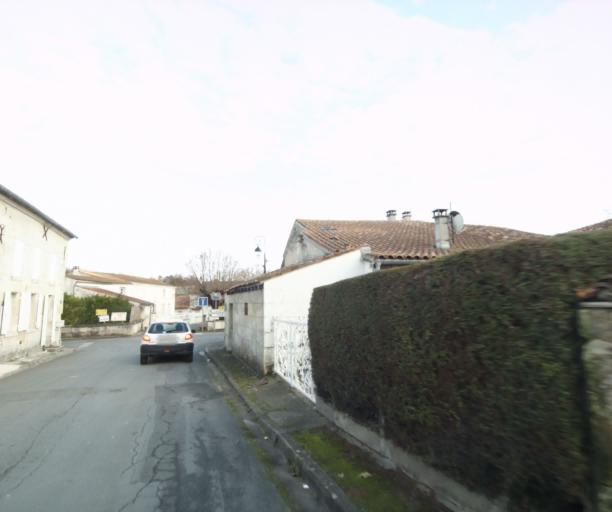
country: FR
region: Poitou-Charentes
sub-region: Departement de la Charente-Maritime
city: Les Gonds
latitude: 45.7064
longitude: -0.5940
